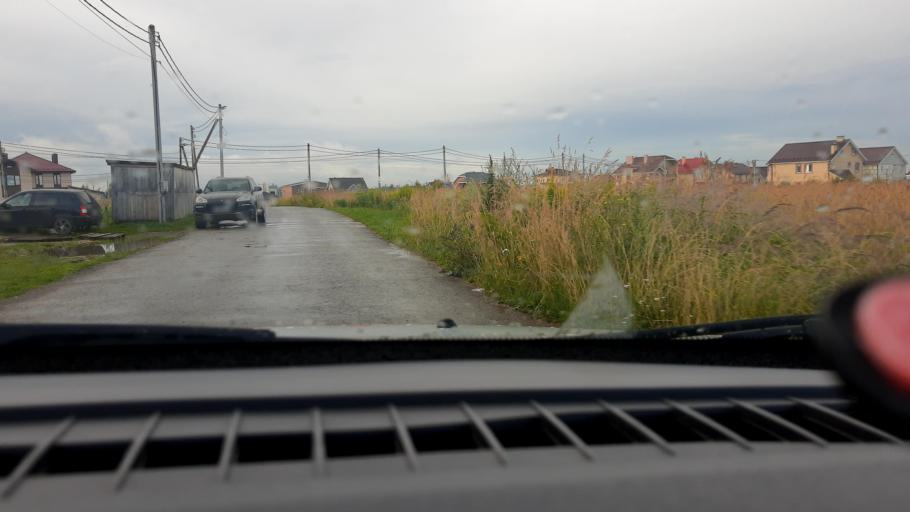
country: RU
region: Nizjnij Novgorod
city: Nizhniy Novgorod
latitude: 56.2175
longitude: 43.9666
